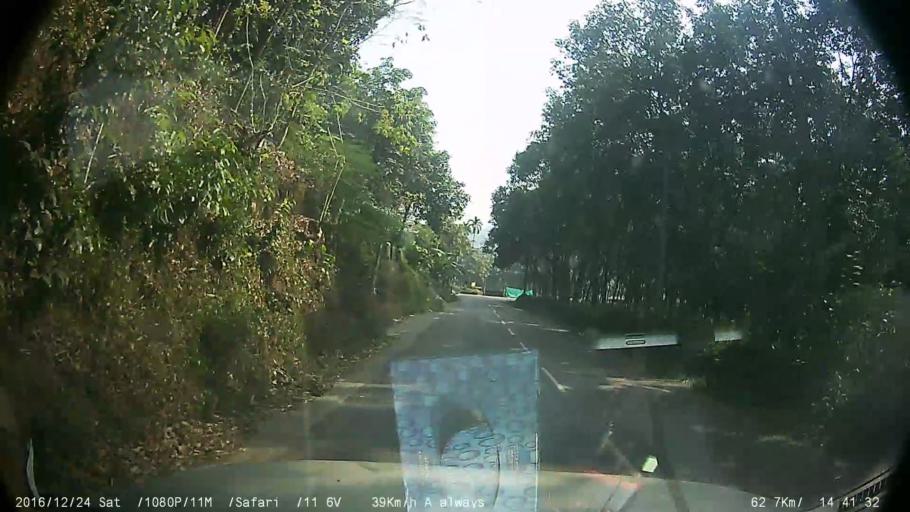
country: IN
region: Kerala
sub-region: Kottayam
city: Lalam
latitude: 9.7811
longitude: 76.7298
